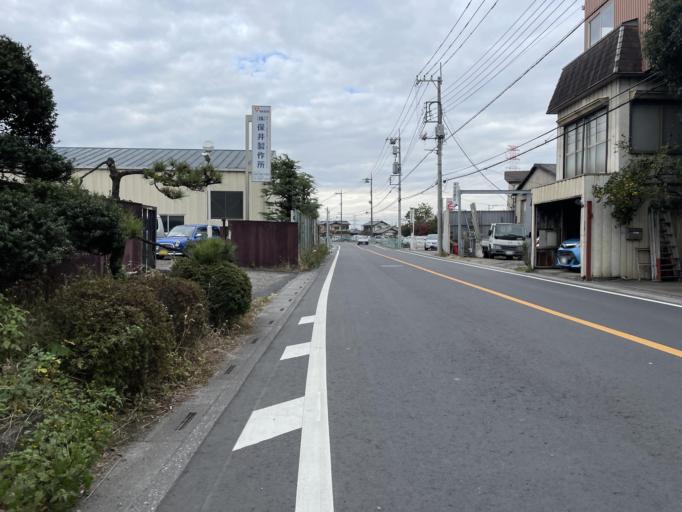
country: JP
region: Saitama
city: Shiraoka
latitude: 36.0340
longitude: 139.6415
